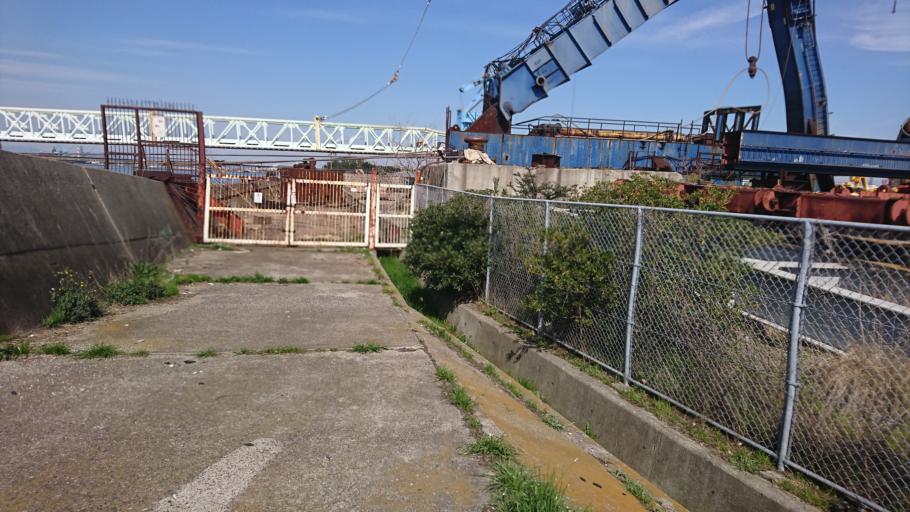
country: JP
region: Hyogo
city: Kakogawacho-honmachi
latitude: 34.6969
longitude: 134.8402
